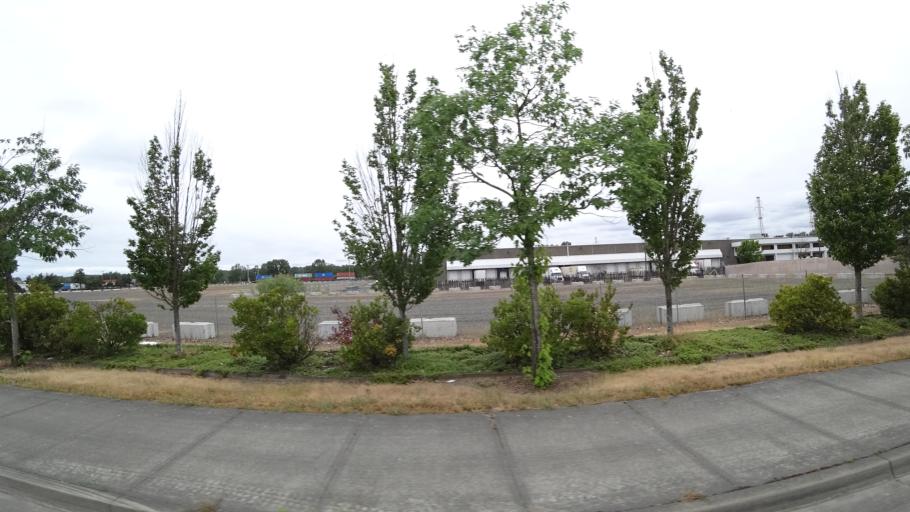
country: US
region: Washington
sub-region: Clark County
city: Vancouver
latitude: 45.6237
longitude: -122.7331
